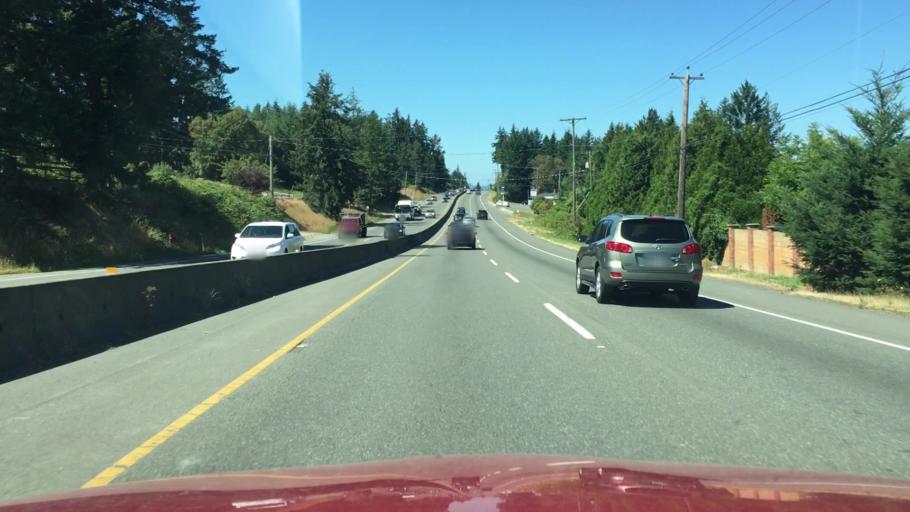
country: CA
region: British Columbia
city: Victoria
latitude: 48.5467
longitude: -123.3913
